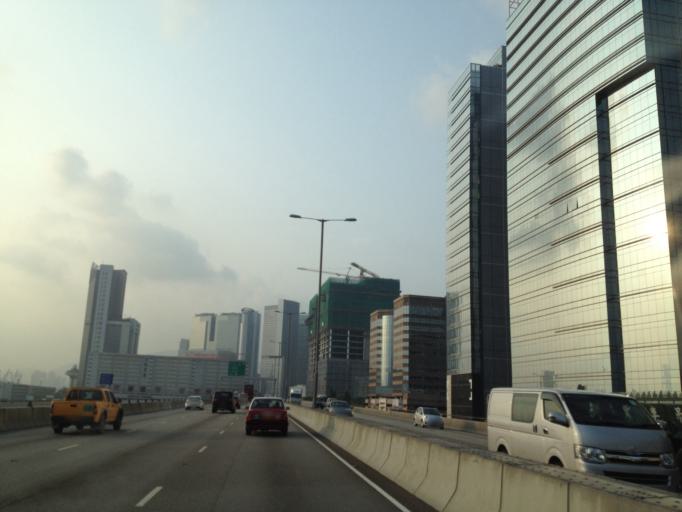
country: HK
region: Kowloon City
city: Kowloon
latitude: 22.3119
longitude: 114.2176
